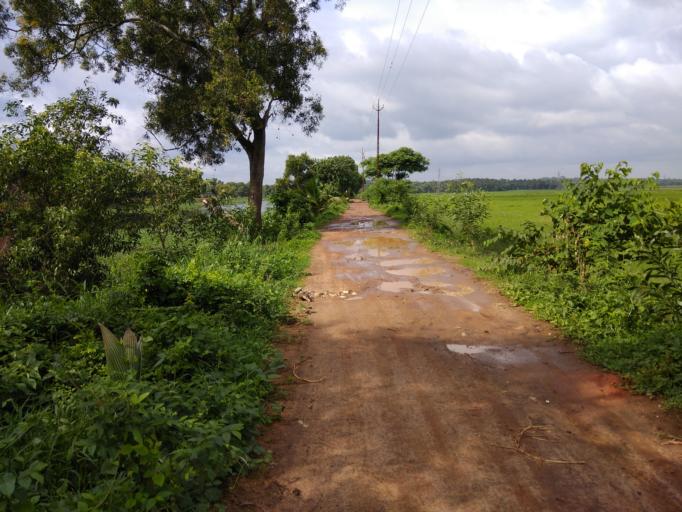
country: IN
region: Kerala
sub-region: Thrissur District
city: Trichur
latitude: 10.5417
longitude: 76.1783
